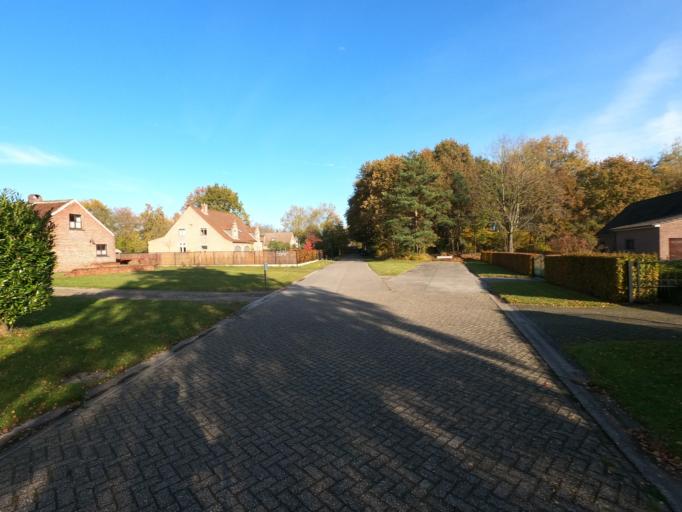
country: BE
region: Flanders
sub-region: Provincie Antwerpen
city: Brasschaat
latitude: 51.3404
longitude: 4.5418
